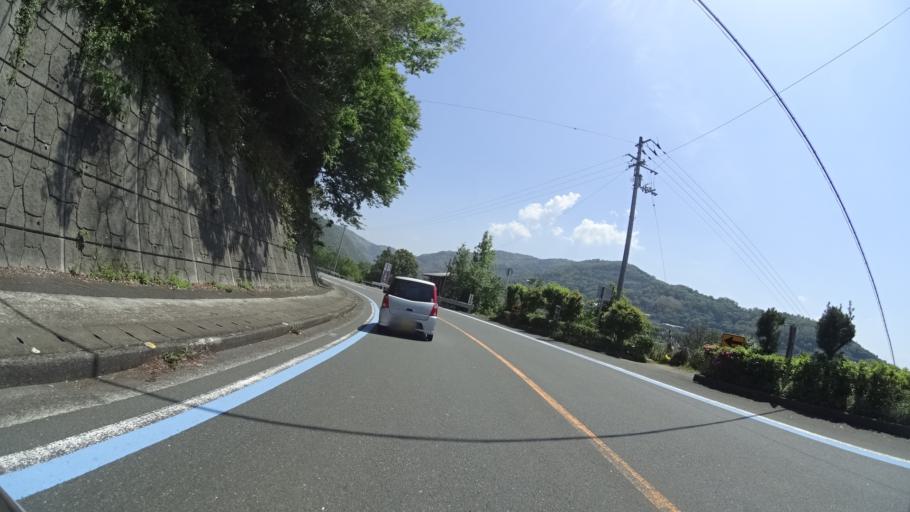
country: JP
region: Ehime
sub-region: Nishiuwa-gun
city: Ikata-cho
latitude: 33.4894
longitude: 132.3504
